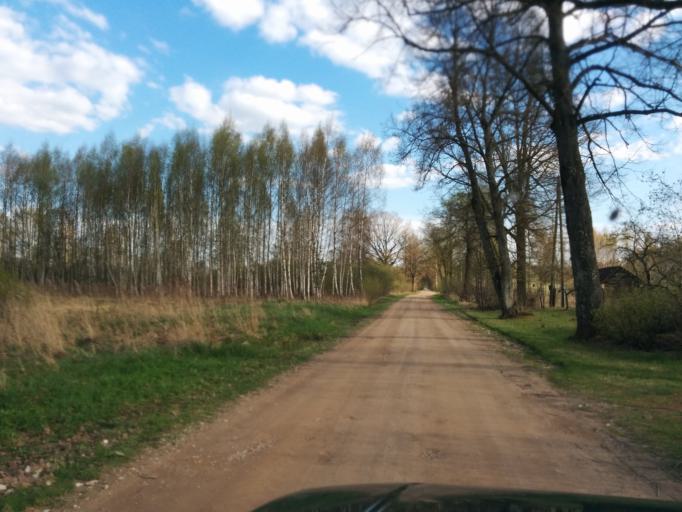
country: LV
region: Jelgava
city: Jelgava
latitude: 56.6689
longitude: 23.6604
